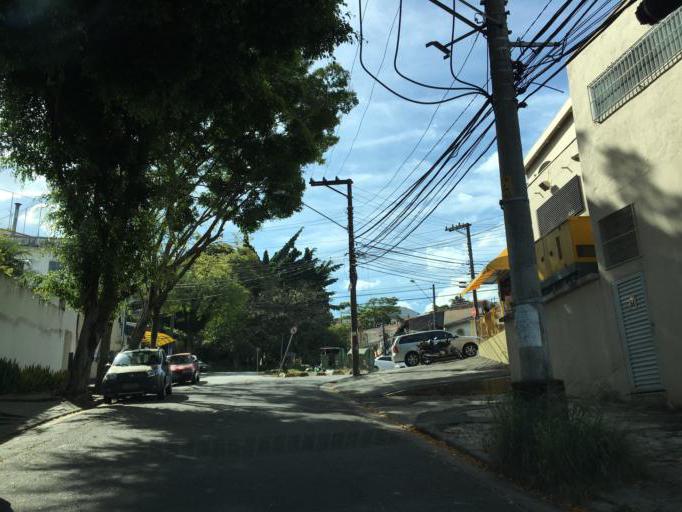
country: BR
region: Sao Paulo
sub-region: Taboao Da Serra
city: Taboao da Serra
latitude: -23.5800
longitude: -46.7384
